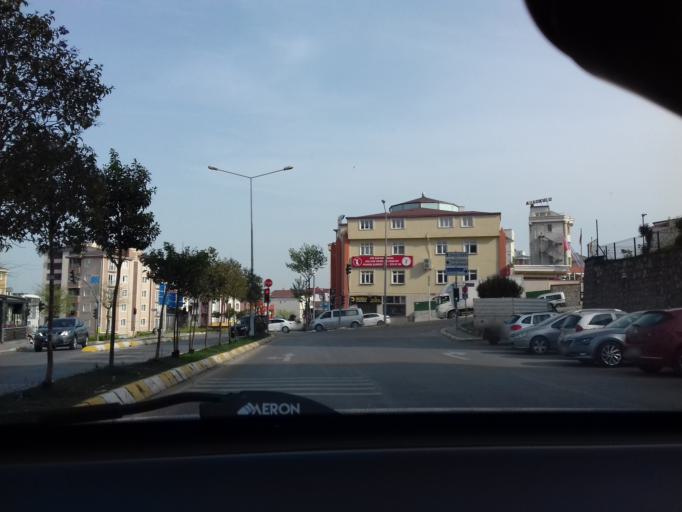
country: TR
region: Istanbul
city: Pendik
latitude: 40.9099
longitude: 29.2800
